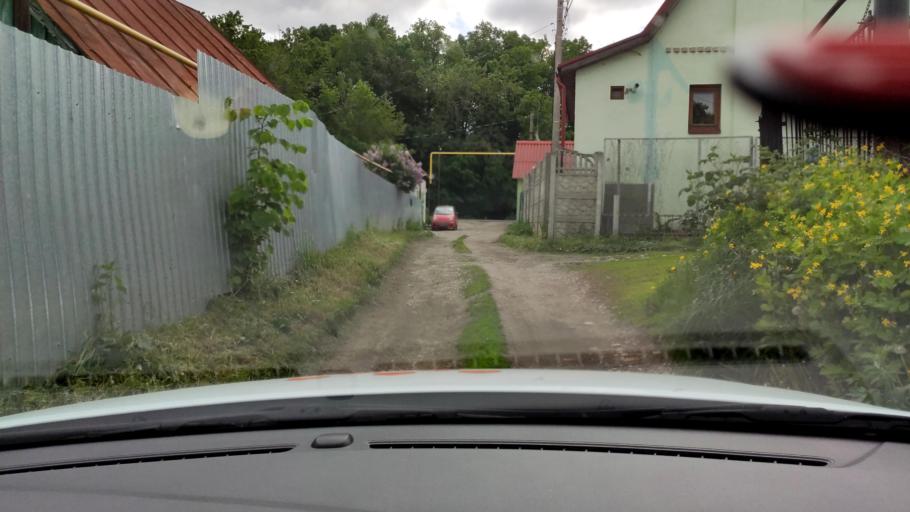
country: RU
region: Tatarstan
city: Staroye Arakchino
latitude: 55.8012
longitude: 48.9842
